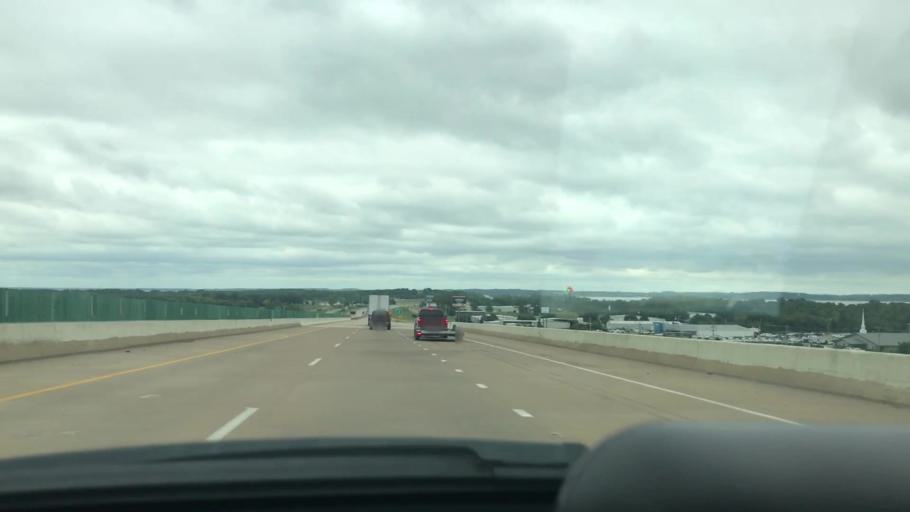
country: US
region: Oklahoma
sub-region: McIntosh County
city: Eufaula
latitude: 35.2925
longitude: -95.5931
